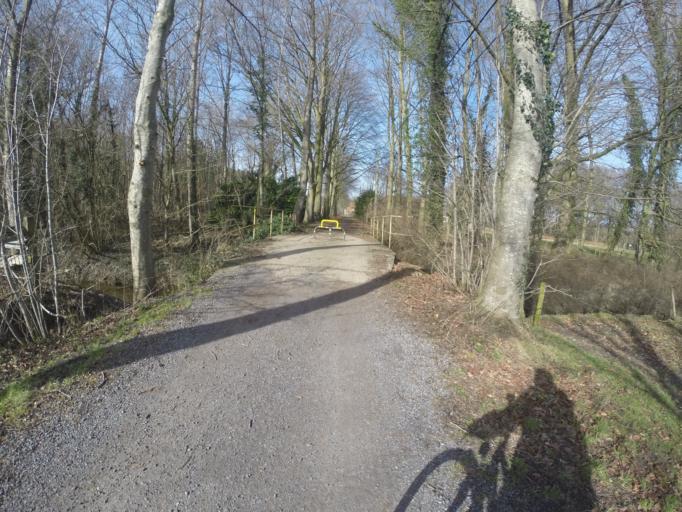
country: BE
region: Flanders
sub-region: Provincie West-Vlaanderen
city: Oostkamp
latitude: 51.1299
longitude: 3.2414
